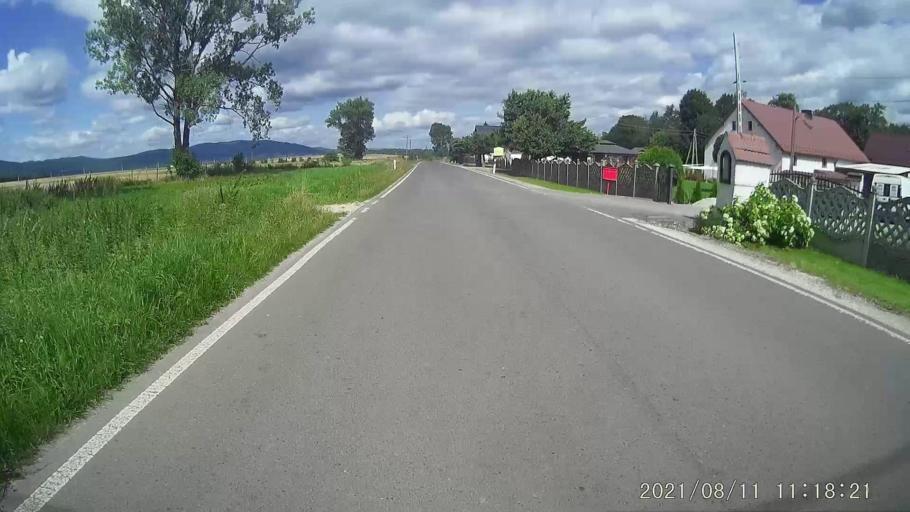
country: PL
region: Lower Silesian Voivodeship
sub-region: Powiat klodzki
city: Bystrzyca Klodzka
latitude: 50.2759
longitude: 16.6861
